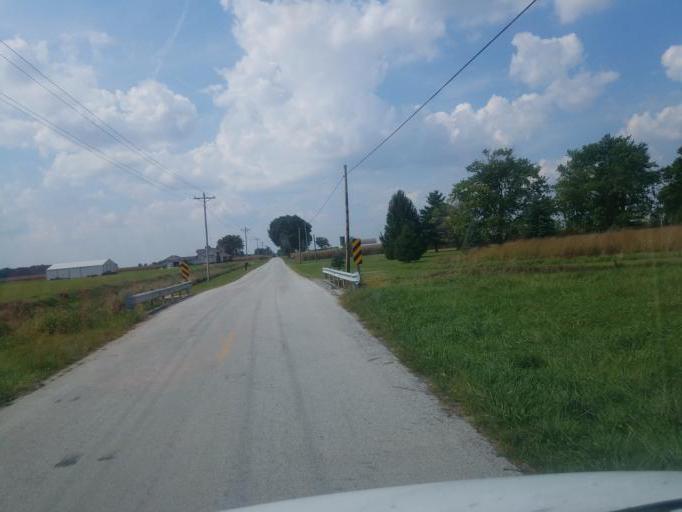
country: US
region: Ohio
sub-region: Hardin County
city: Kenton
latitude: 40.6425
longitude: -83.7335
